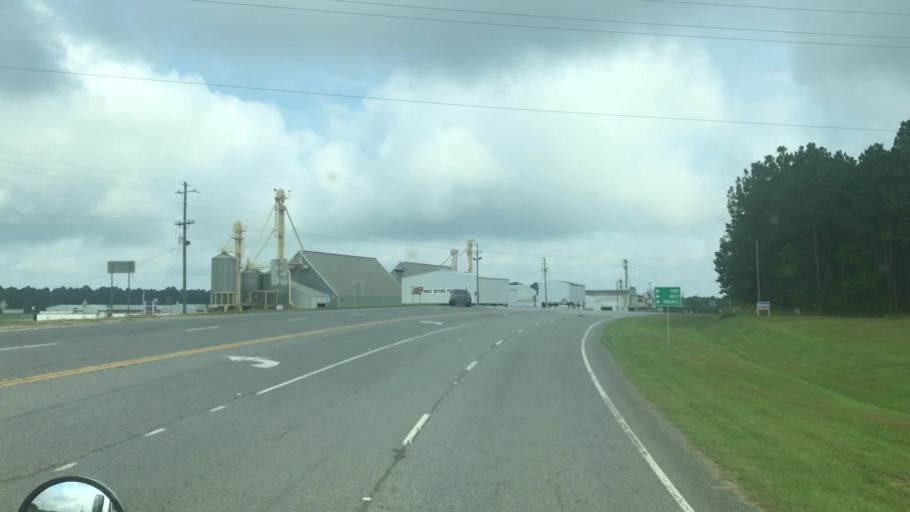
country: US
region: Georgia
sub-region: Miller County
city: Colquitt
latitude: 31.1699
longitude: -84.7547
